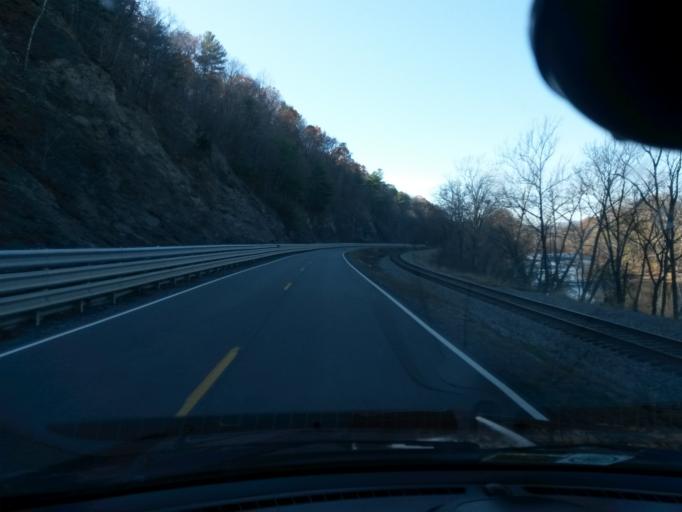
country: US
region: Virginia
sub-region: Alleghany County
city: Clifton Forge
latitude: 37.6556
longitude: -79.8006
